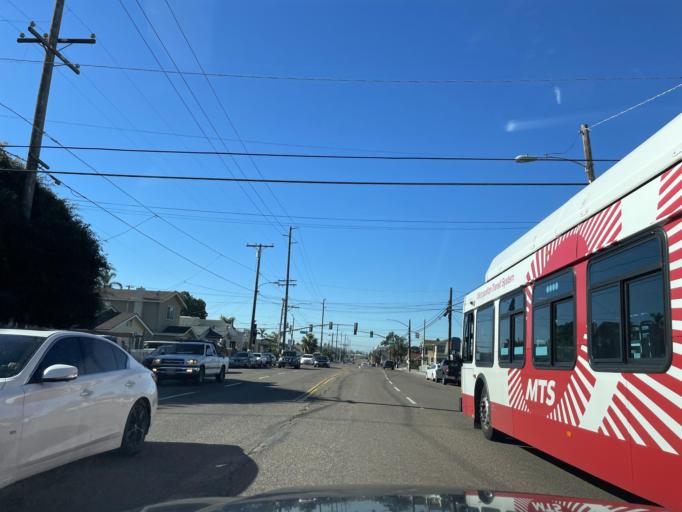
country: US
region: California
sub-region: San Diego County
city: National City
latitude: 32.6756
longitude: -117.1011
